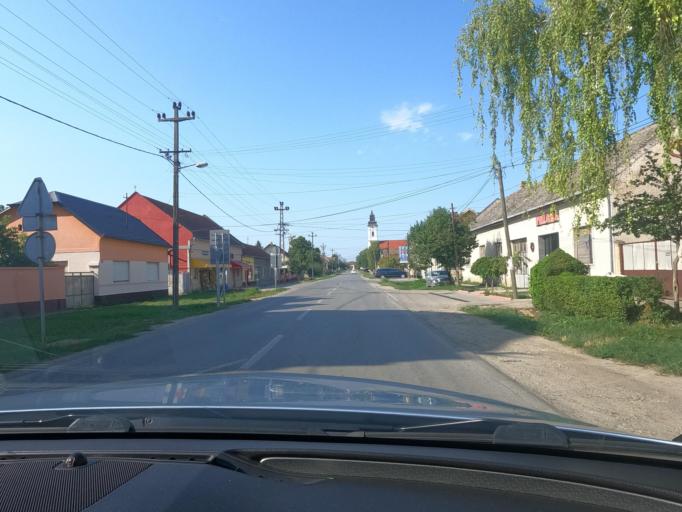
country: RS
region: Autonomna Pokrajina Vojvodina
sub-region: Juznobacki Okrug
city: Kovilj
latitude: 45.2258
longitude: 20.0213
